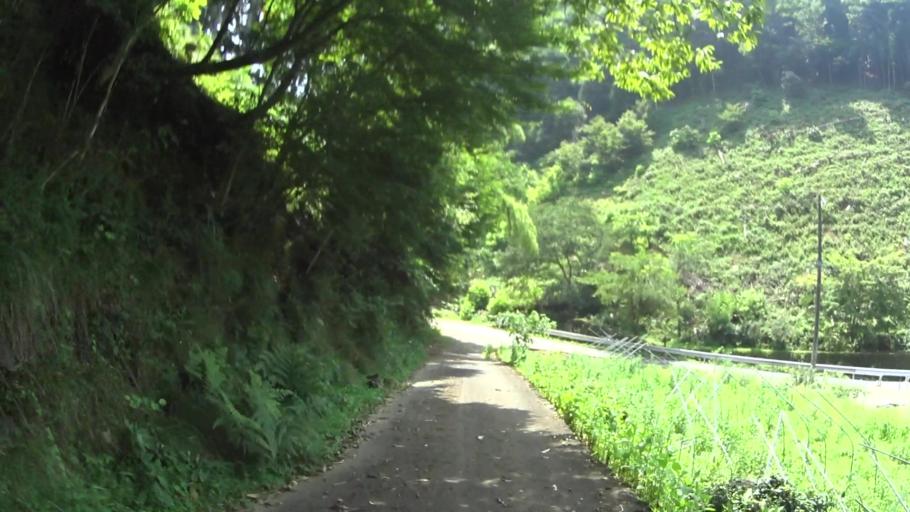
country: JP
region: Kyoto
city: Maizuru
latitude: 35.3254
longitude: 135.4607
